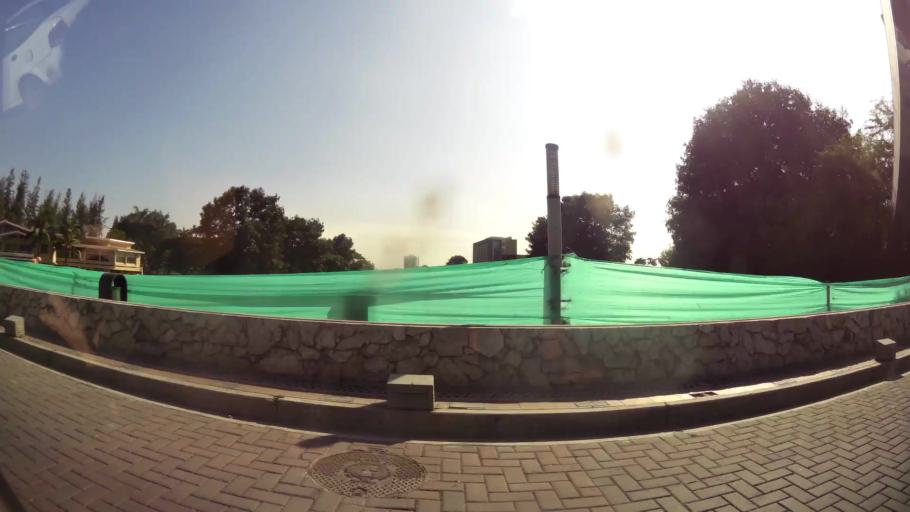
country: EC
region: Guayas
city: Guayaquil
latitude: -2.1771
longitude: -79.9035
